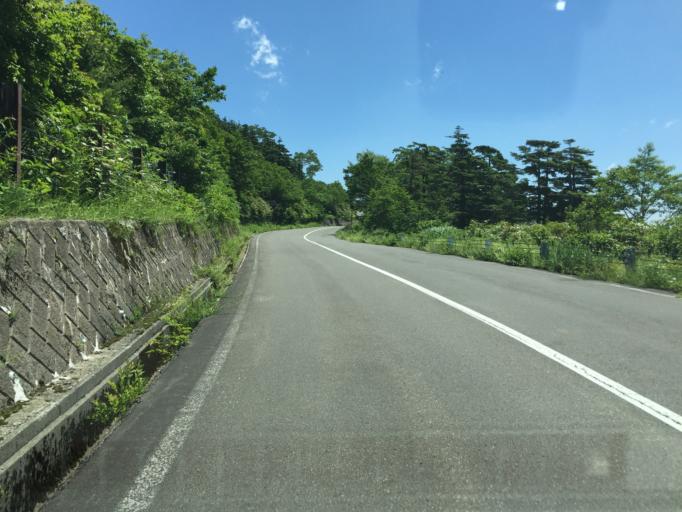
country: JP
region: Fukushima
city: Inawashiro
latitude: 37.6916
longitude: 140.2389
